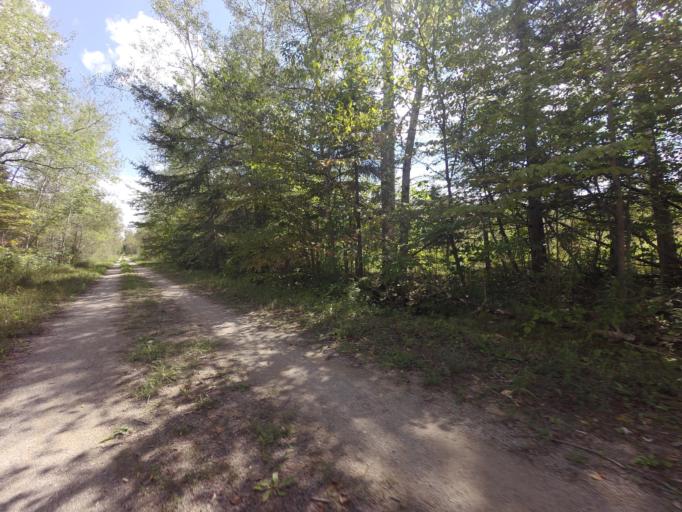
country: CA
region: Ontario
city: Orangeville
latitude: 43.7881
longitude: -80.2456
